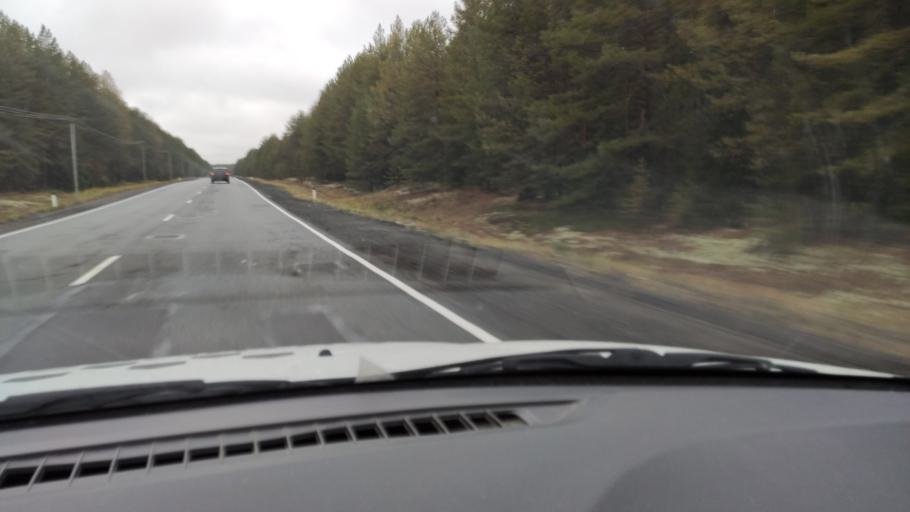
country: RU
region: Kirov
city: Belaya Kholunitsa
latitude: 58.9072
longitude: 51.0088
